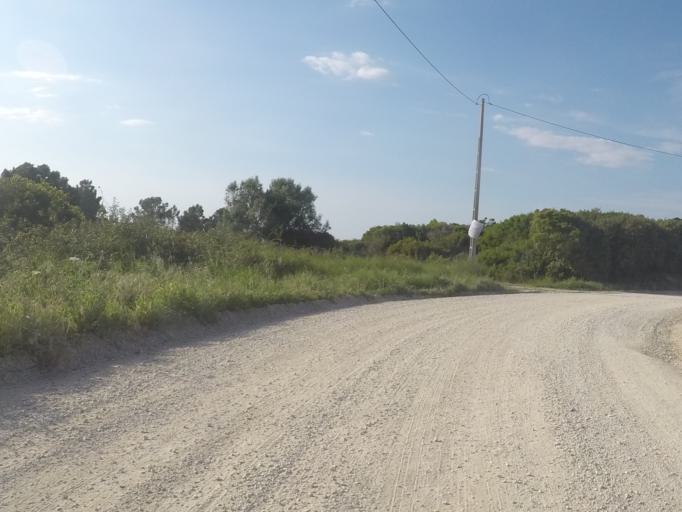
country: PT
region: Setubal
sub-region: Sesimbra
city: Sesimbra
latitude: 38.4349
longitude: -9.1886
